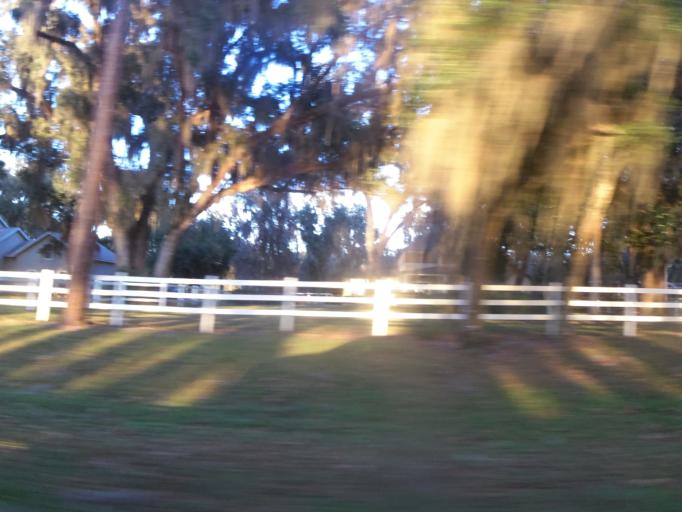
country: US
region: Florida
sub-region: Clay County
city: Green Cove Springs
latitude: 29.9046
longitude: -81.5897
